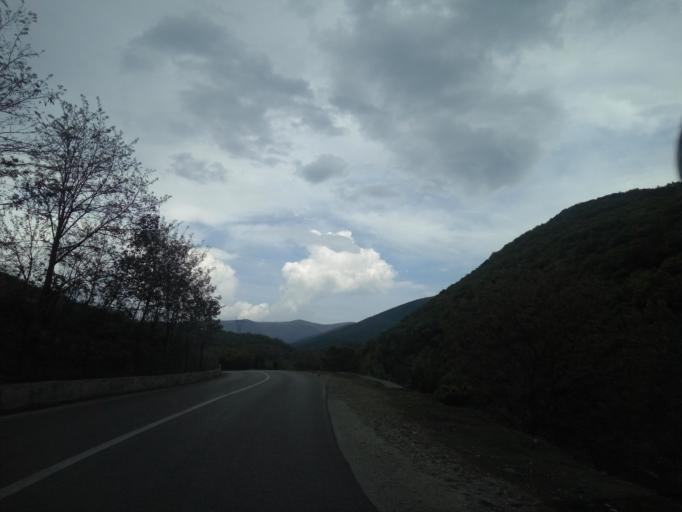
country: AL
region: Kukes
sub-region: Rrethi i Tropojes
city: Llugaj
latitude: 42.3843
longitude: 20.1411
